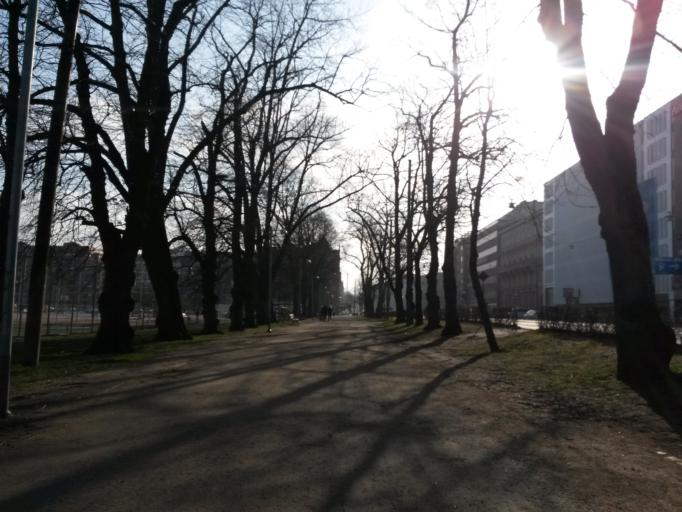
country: SE
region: Vaestra Goetaland
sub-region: Goteborg
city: Goeteborg
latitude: 57.7009
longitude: 11.9774
